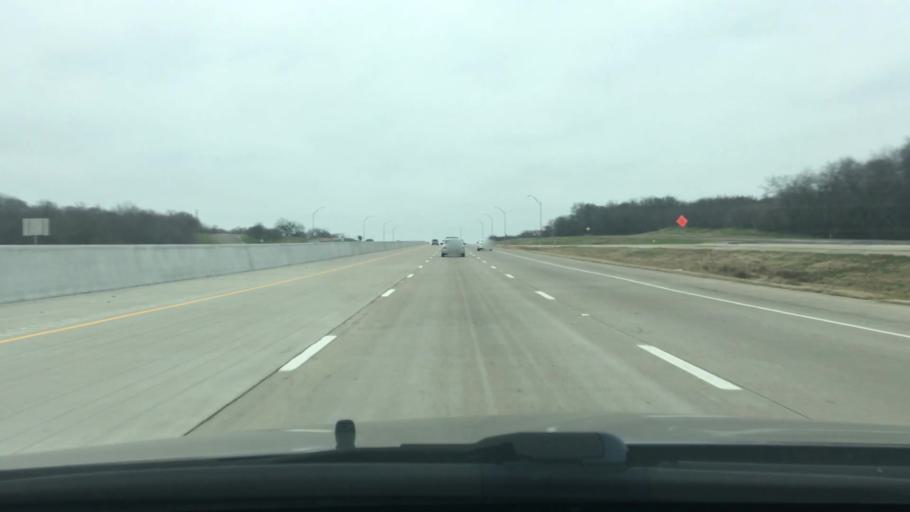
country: US
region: Texas
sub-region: Freestone County
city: Wortham
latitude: 31.9084
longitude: -96.3899
